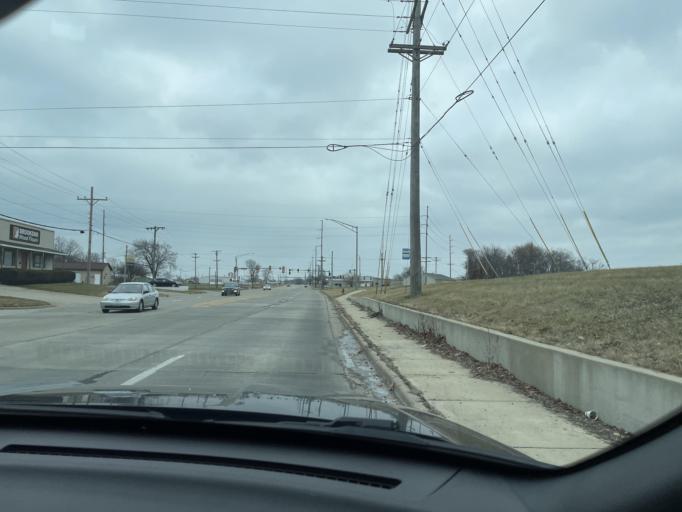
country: US
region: Illinois
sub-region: Sangamon County
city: Grandview
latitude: 39.7947
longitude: -89.6150
